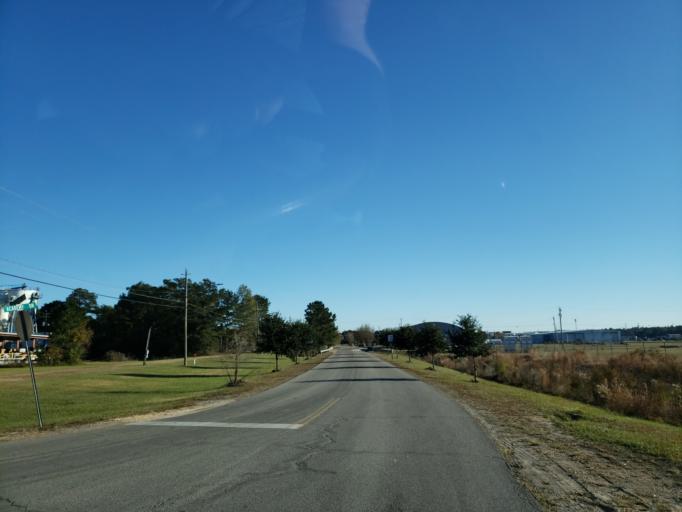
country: US
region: Mississippi
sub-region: Forrest County
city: Hattiesburg
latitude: 31.2732
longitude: -89.2537
